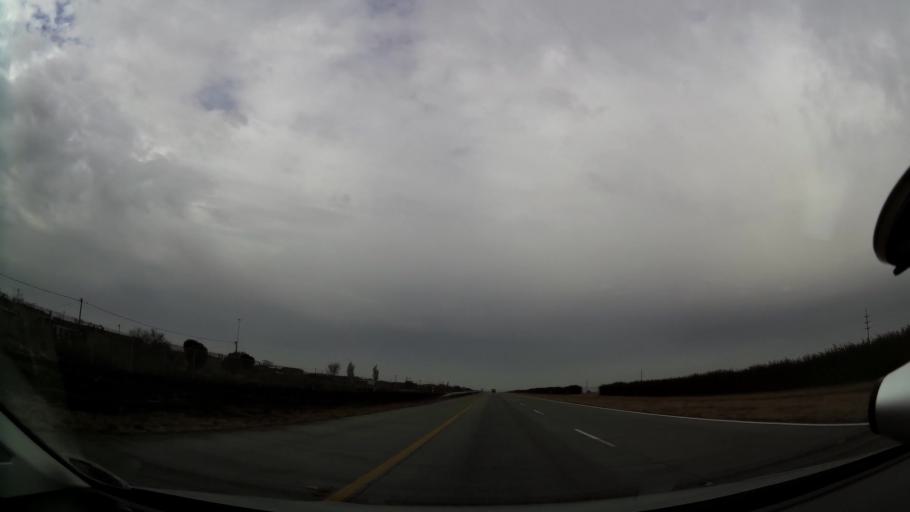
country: ZA
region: Gauteng
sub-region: City of Johannesburg Metropolitan Municipality
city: Orange Farm
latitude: -26.5091
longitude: 27.8123
